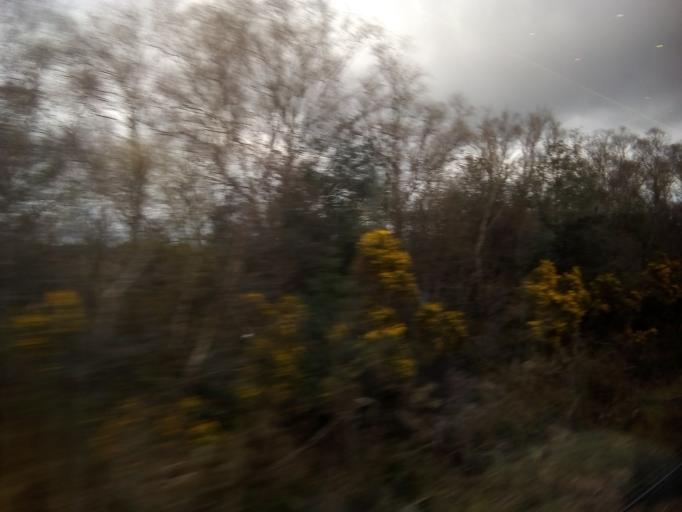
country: IE
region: Leinster
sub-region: An Longfort
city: Longford
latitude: 53.8053
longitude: -7.8600
